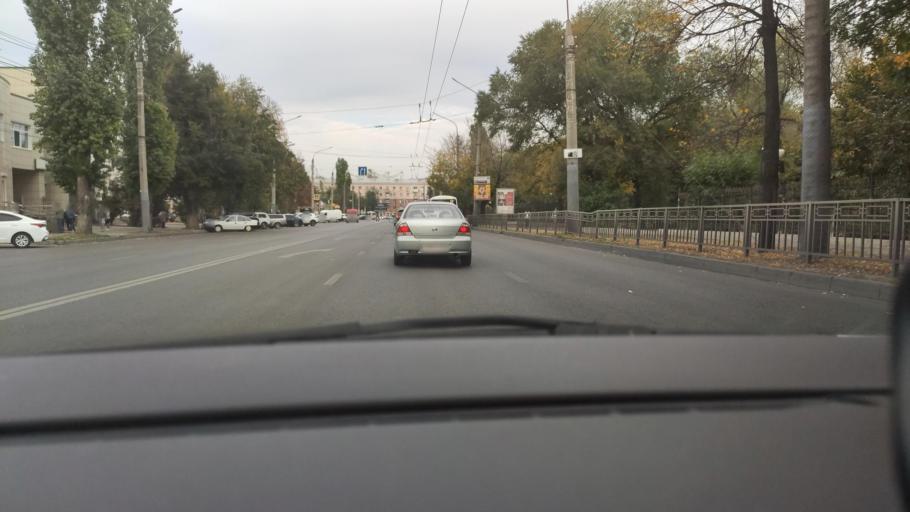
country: RU
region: Voronezj
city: Voronezh
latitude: 51.6557
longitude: 39.1819
